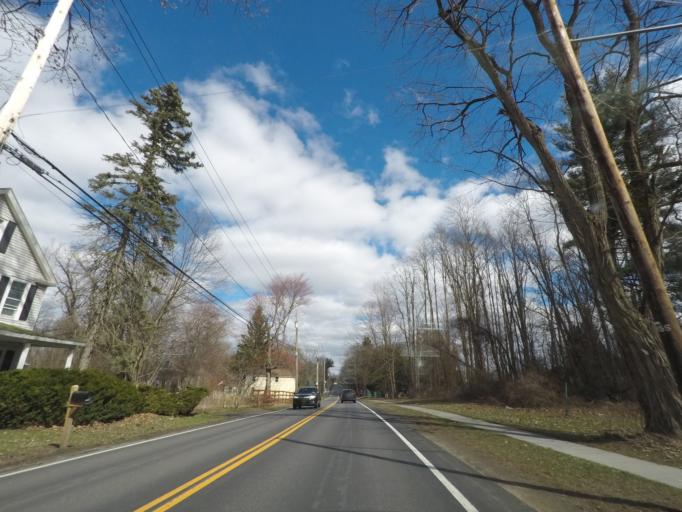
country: US
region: New York
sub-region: Albany County
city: Delmar
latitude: 42.6016
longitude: -73.7988
